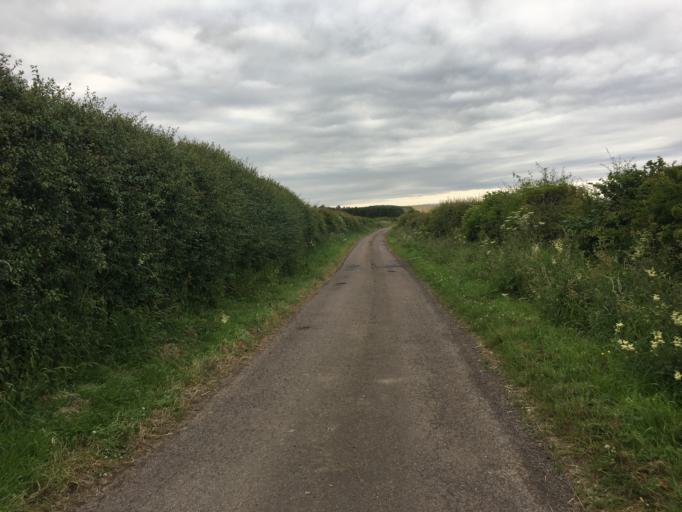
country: GB
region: England
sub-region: Northumberland
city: Lowick
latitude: 55.6573
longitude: -1.9042
